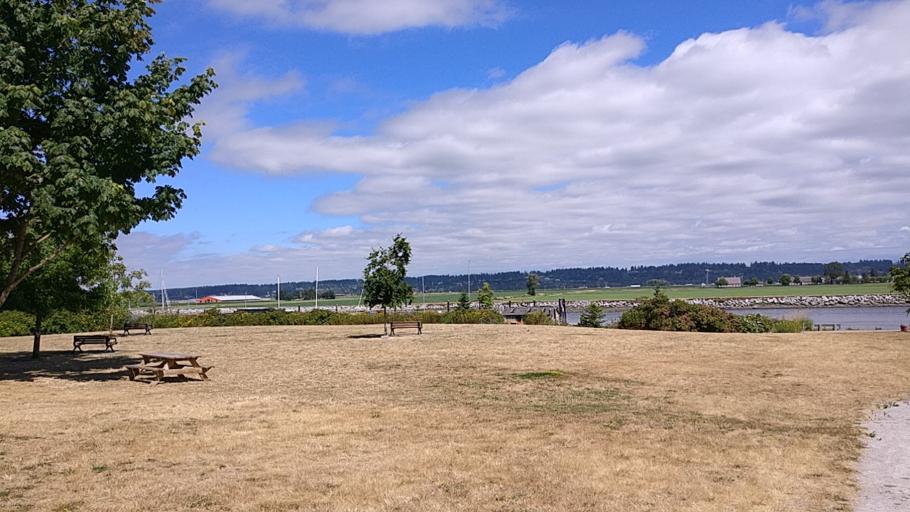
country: CA
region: British Columbia
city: Surrey
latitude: 49.0653
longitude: -122.8415
